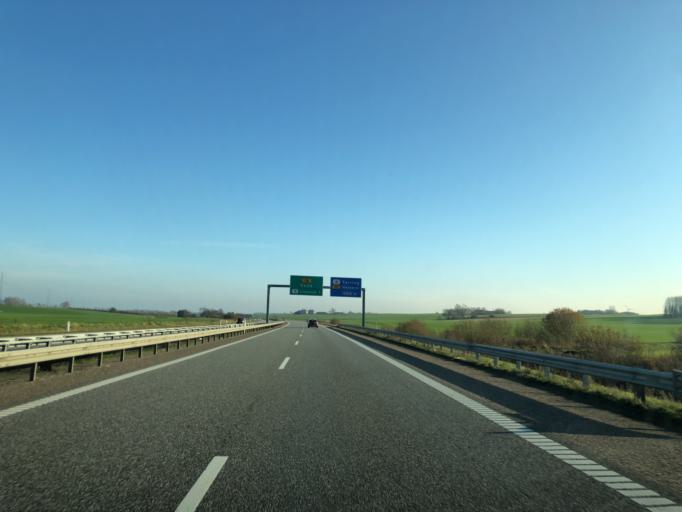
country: DK
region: Central Jutland
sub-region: Hedensted Kommune
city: Torring
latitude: 55.8355
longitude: 9.4527
